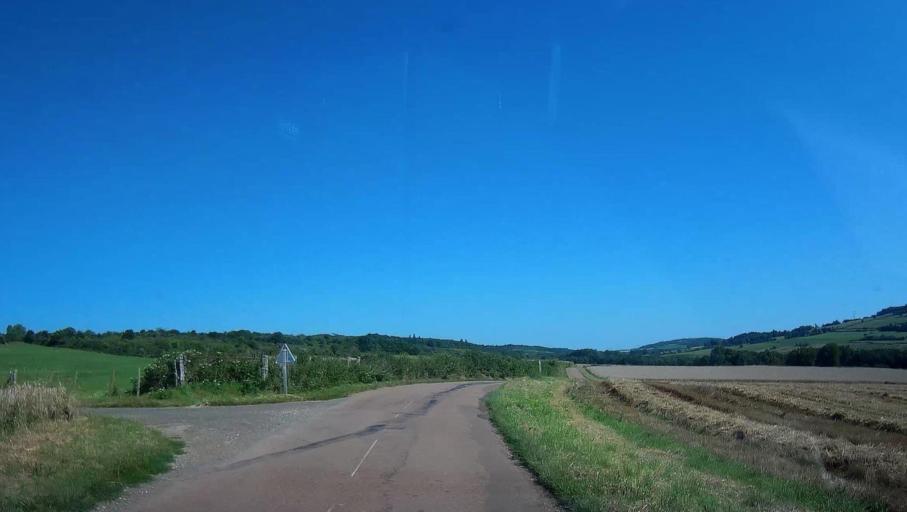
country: FR
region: Bourgogne
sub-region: Departement de Saone-et-Loire
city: Couches
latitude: 46.8912
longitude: 4.5911
